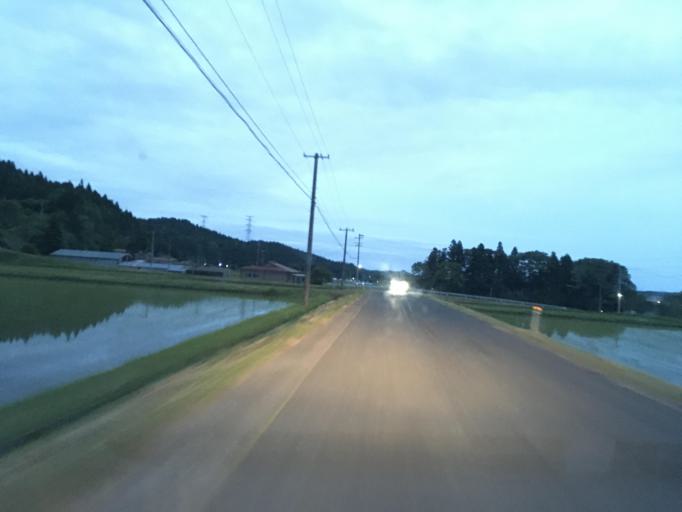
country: JP
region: Miyagi
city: Furukawa
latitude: 38.7702
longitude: 140.8959
